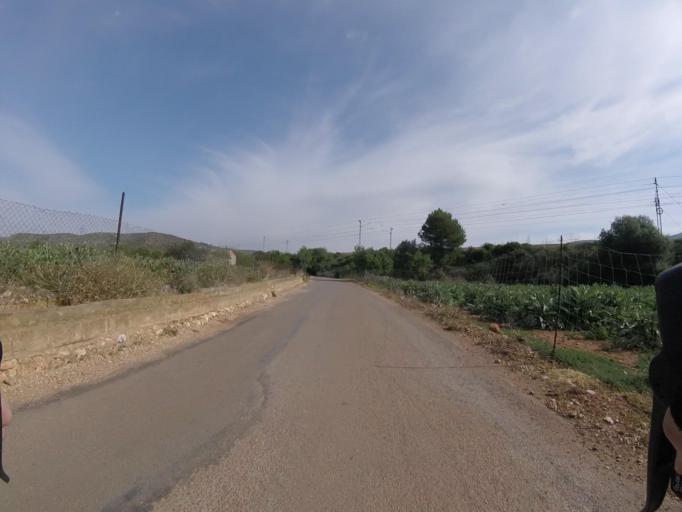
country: ES
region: Valencia
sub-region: Provincia de Castello
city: Alcoceber
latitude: 40.2667
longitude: 0.2530
